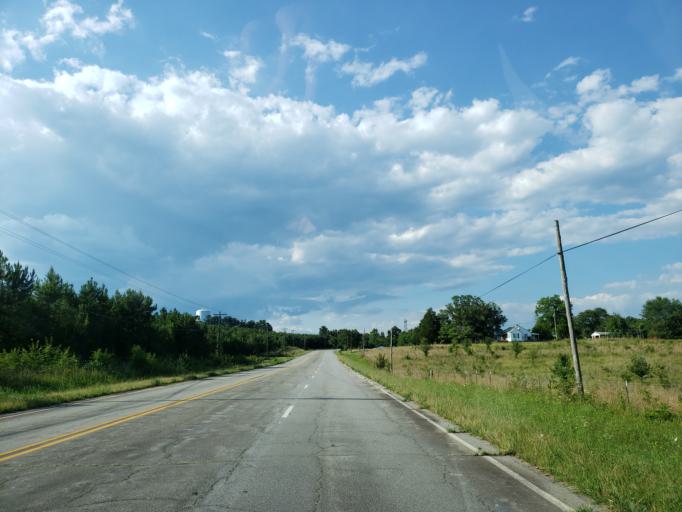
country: US
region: Georgia
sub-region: Haralson County
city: Buchanan
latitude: 33.7745
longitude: -85.1698
